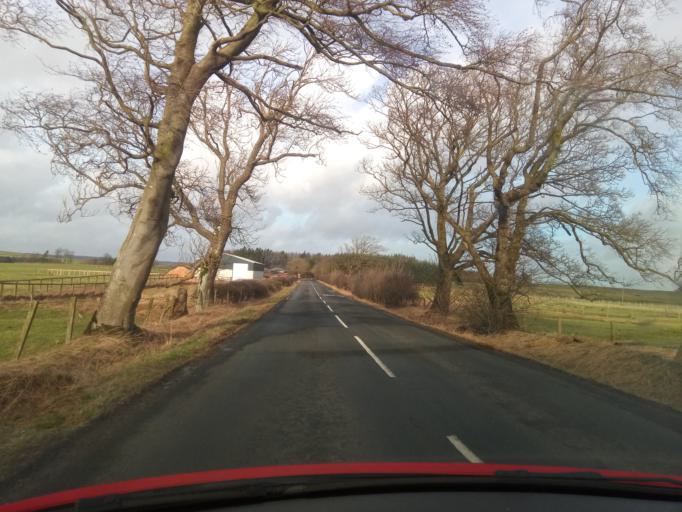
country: GB
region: England
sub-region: Northumberland
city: Rothley
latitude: 55.1066
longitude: -2.0089
